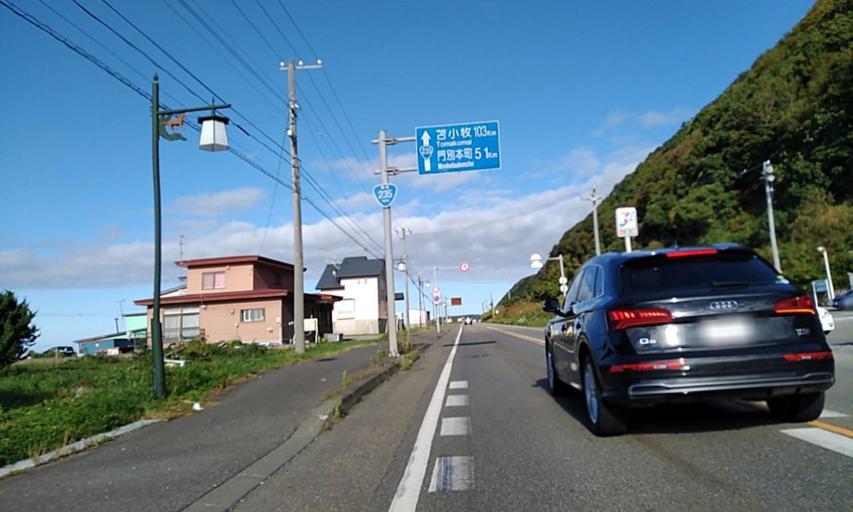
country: JP
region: Hokkaido
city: Shizunai-furukawacho
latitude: 42.2552
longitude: 142.5357
